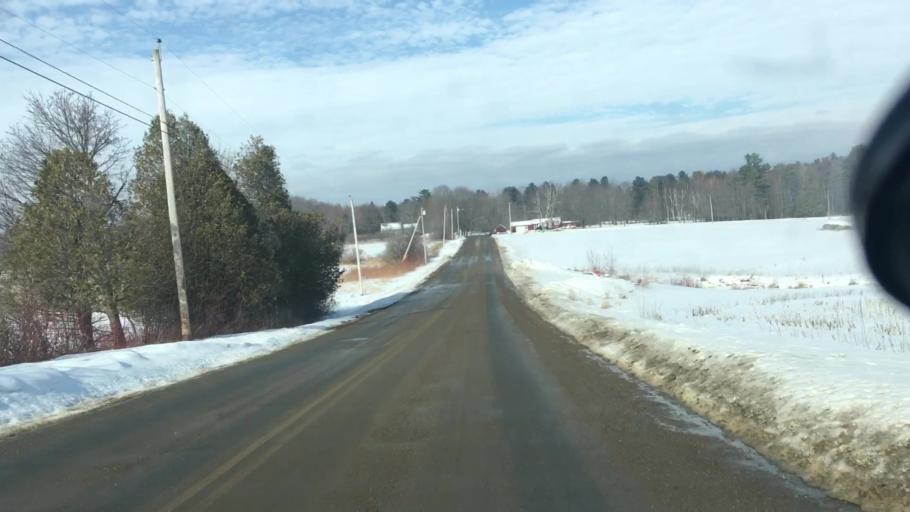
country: US
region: Maine
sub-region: Penobscot County
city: Levant
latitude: 44.8595
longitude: -68.8790
